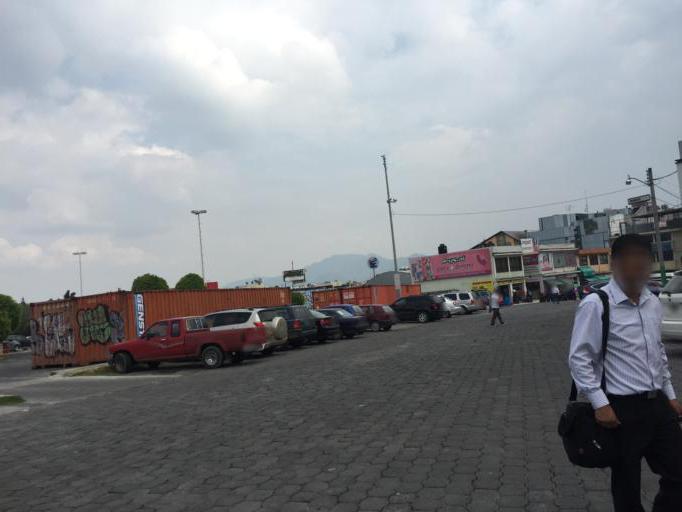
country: MX
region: Mexico
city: Cuautitlan Izcalli
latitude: 19.6539
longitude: -99.2076
